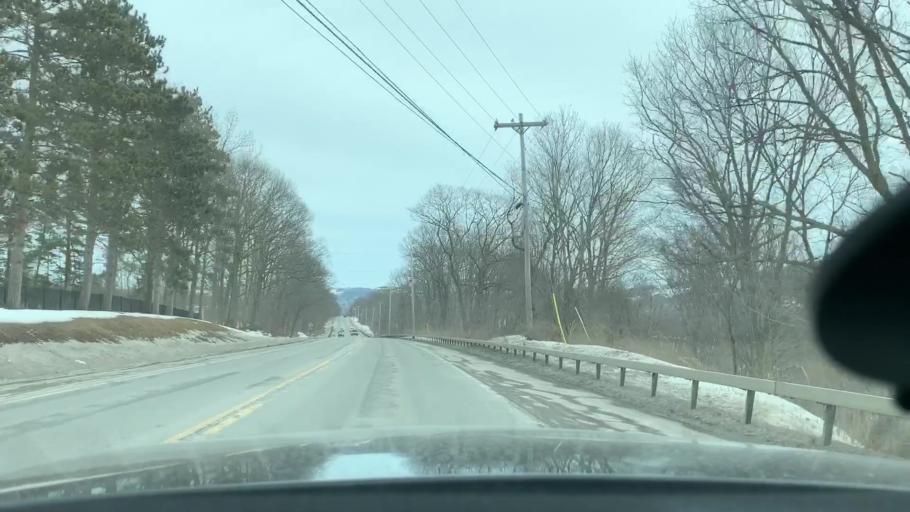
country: US
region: New York
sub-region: Herkimer County
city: Herkimer
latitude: 43.0248
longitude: -74.9381
